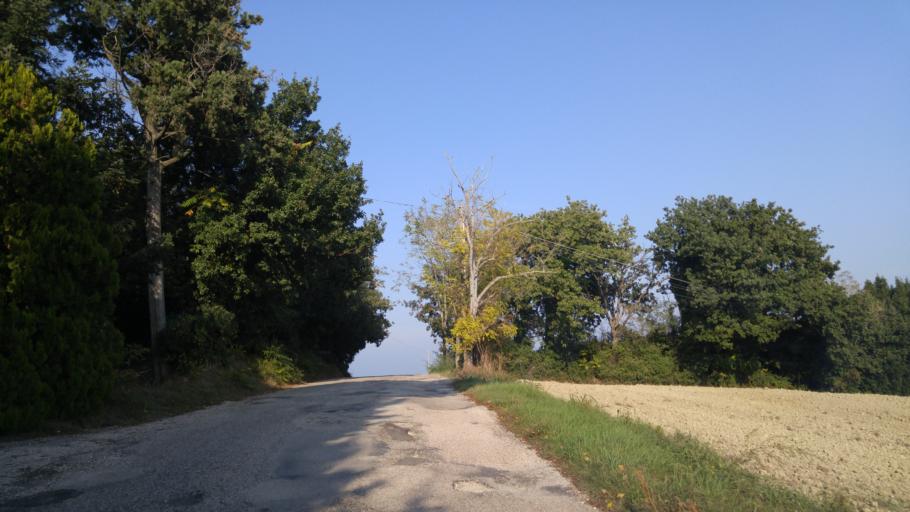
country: IT
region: The Marches
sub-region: Provincia di Pesaro e Urbino
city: Fenile
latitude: 43.8710
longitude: 12.9682
